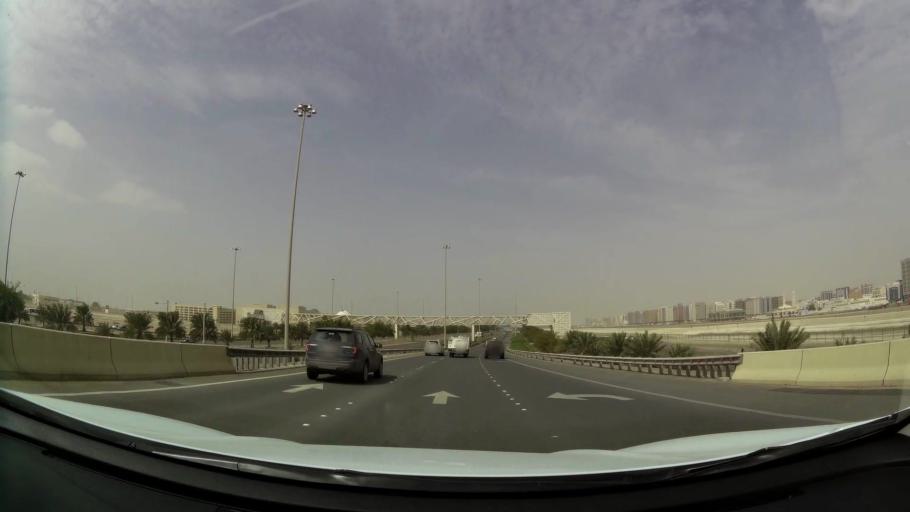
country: AE
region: Abu Dhabi
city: Abu Dhabi
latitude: 24.3255
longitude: 54.5276
